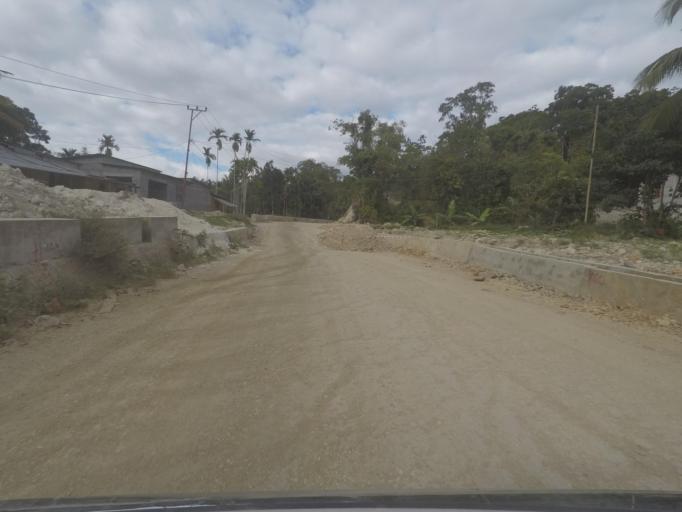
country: TL
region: Baucau
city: Venilale
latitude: -8.6041
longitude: 126.3820
